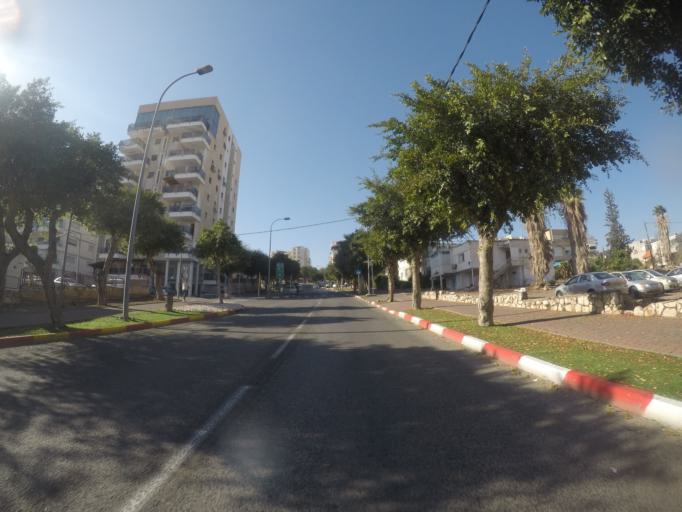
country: IL
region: Northern District
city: Tiberias
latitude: 32.7954
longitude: 35.5285
